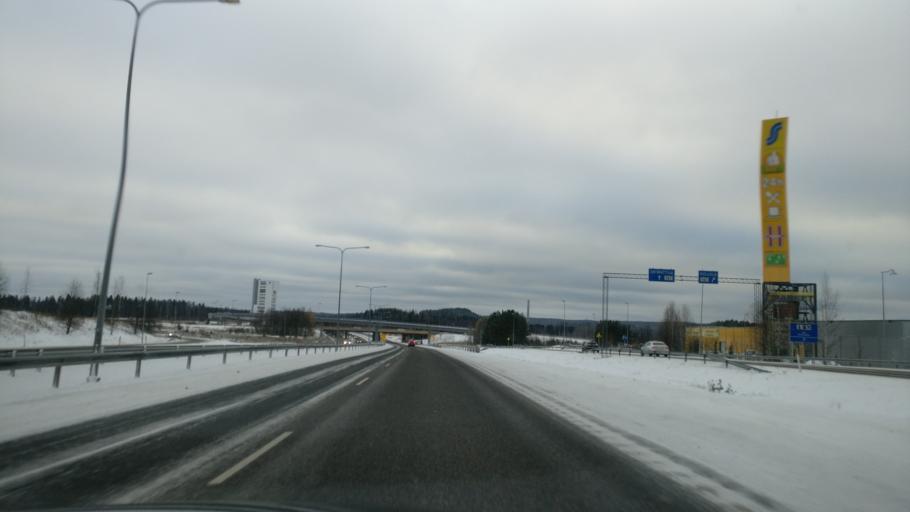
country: FI
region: Paijanne Tavastia
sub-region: Lahti
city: Lahti
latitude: 60.9343
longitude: 25.6402
